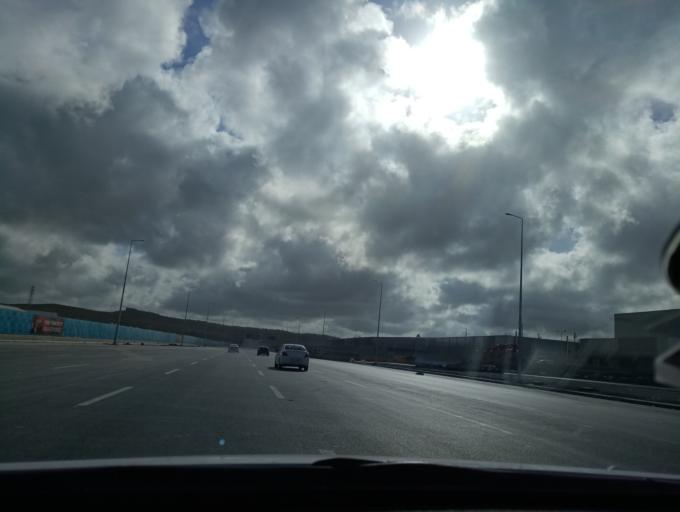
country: TR
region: Istanbul
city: Durusu
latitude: 41.2534
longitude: 28.7389
